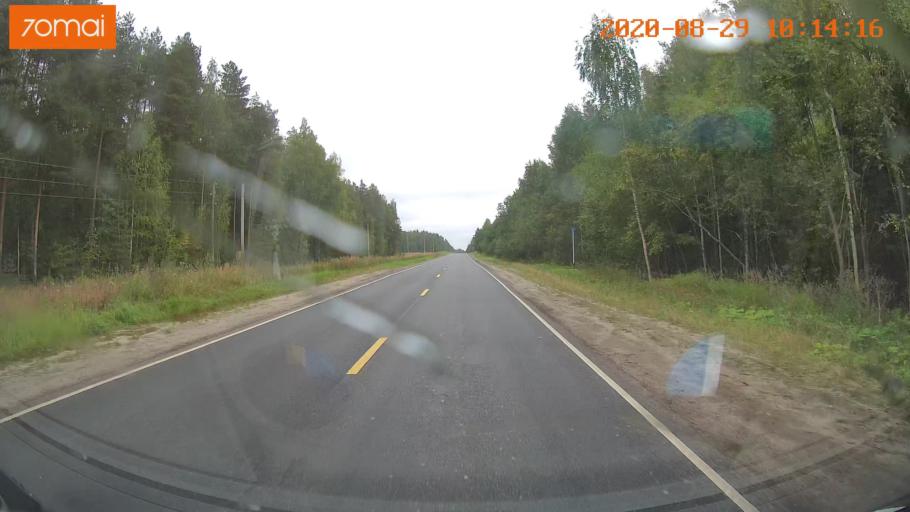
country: RU
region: Ivanovo
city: Yur'yevets
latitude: 57.3545
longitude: 42.7499
